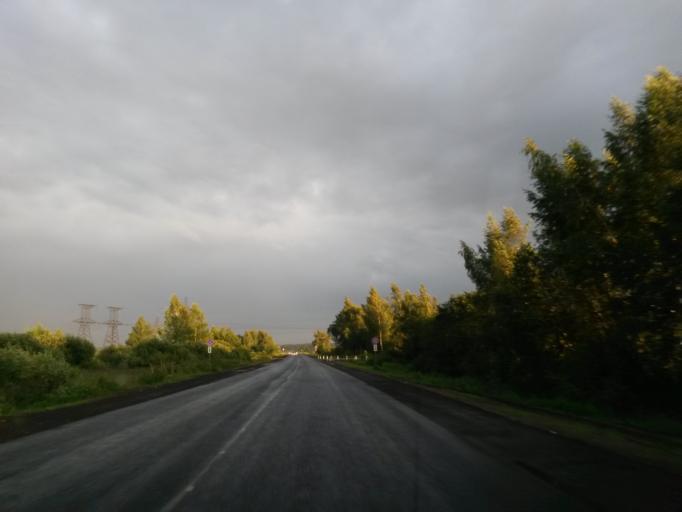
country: RU
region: Jaroslavl
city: Yaroslavl
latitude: 57.5294
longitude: 39.8764
